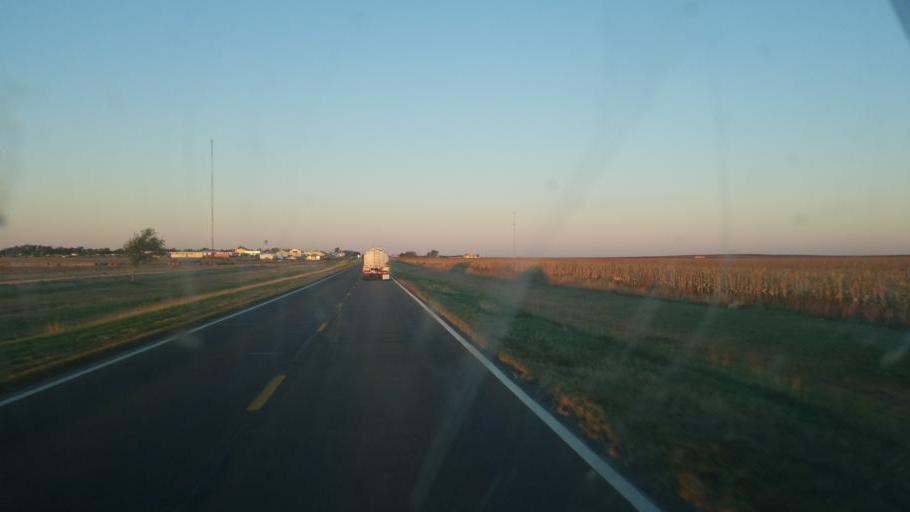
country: US
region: Kansas
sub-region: Wallace County
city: Sharon Springs
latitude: 38.9019
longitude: -101.7334
